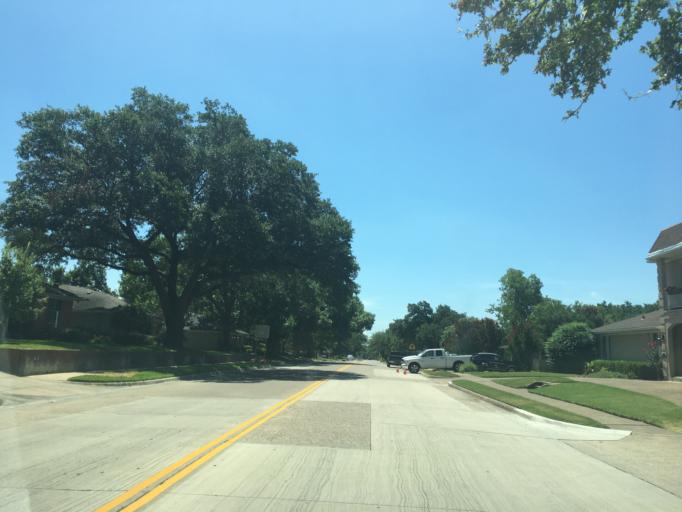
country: US
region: Texas
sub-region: Dallas County
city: Highland Park
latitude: 32.8512
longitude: -96.7142
